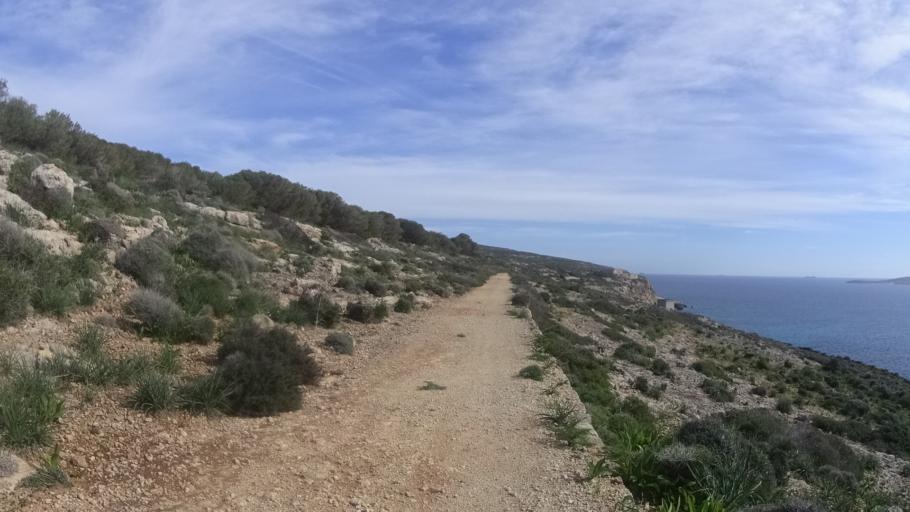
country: MT
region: Il-Qala
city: Qala
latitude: 36.0065
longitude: 14.3421
